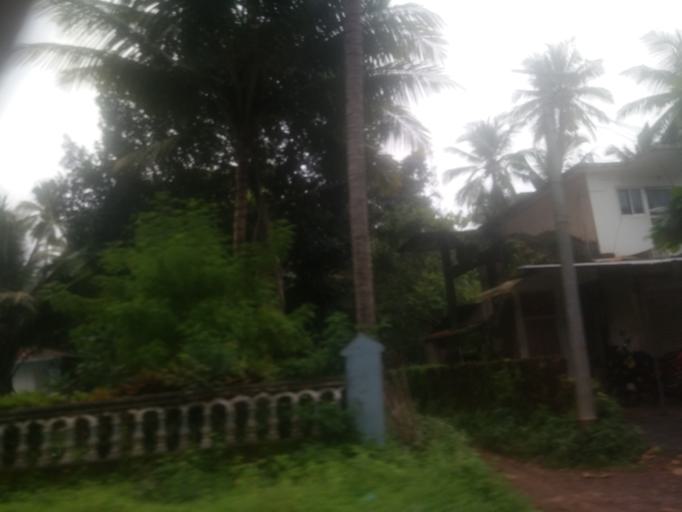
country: IN
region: Goa
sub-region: South Goa
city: Varca
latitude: 15.2093
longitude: 73.9503
